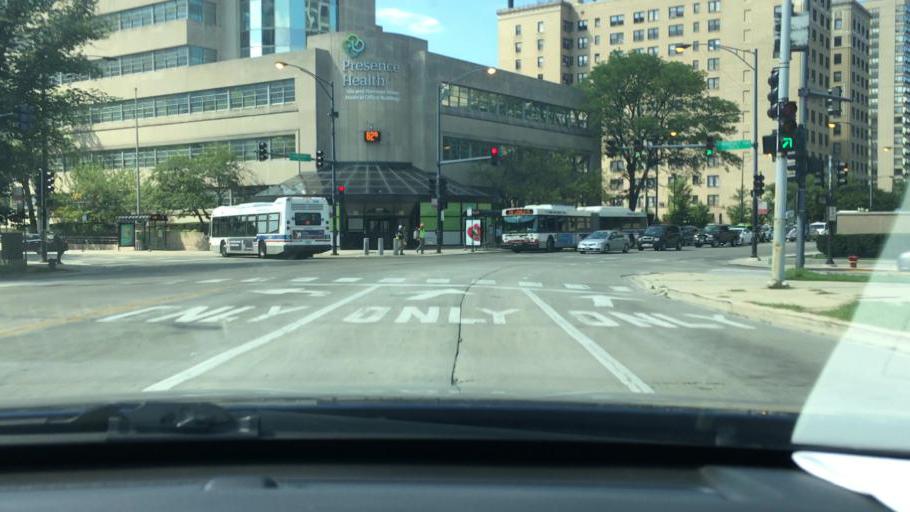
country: US
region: Illinois
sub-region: Cook County
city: Chicago
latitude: 41.9339
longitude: -87.6381
